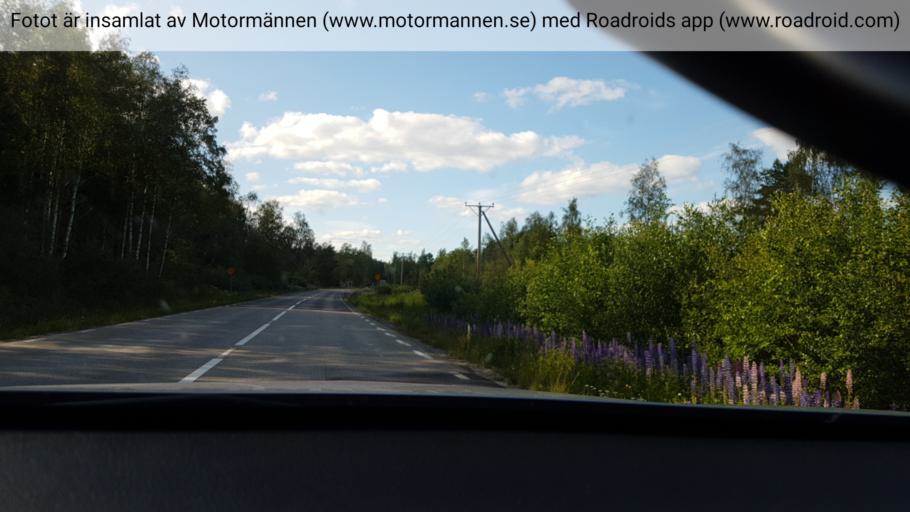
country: SE
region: Vaermland
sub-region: Filipstads Kommun
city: Lesjofors
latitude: 59.9232
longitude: 13.9806
